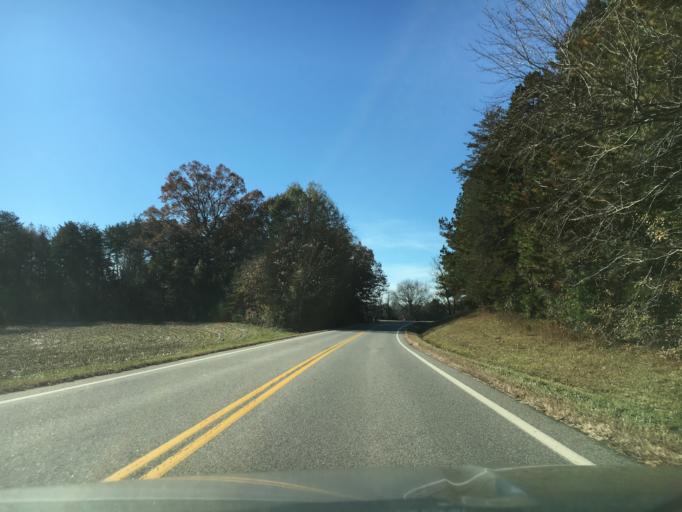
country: US
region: Virginia
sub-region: Cumberland County
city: Cumberland
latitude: 37.5299
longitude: -78.1997
